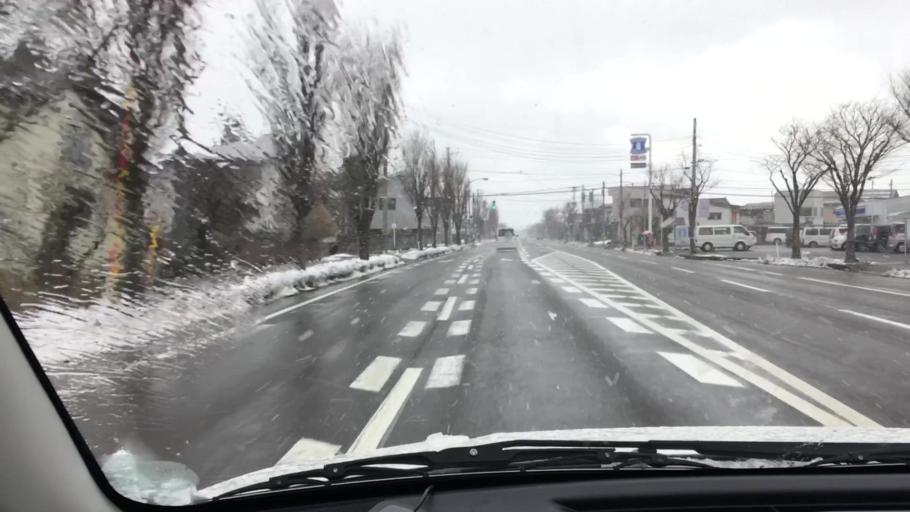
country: JP
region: Niigata
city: Joetsu
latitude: 37.1166
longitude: 138.2330
